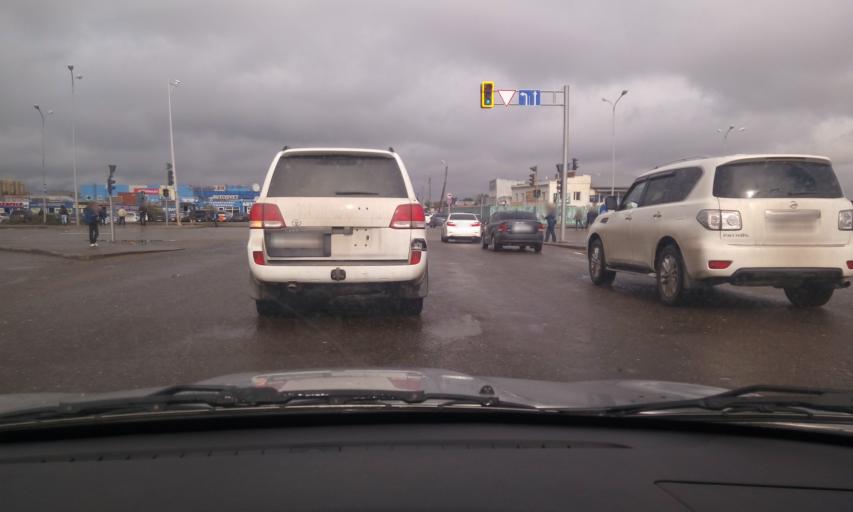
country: KZ
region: Astana Qalasy
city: Astana
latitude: 51.1788
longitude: 71.3822
